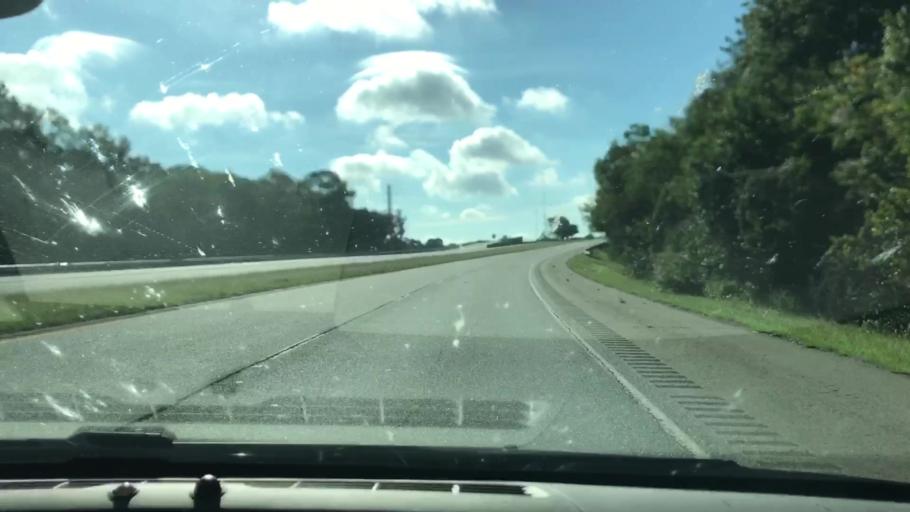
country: US
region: Georgia
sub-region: Dougherty County
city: Albany
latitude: 31.6107
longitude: -84.1612
